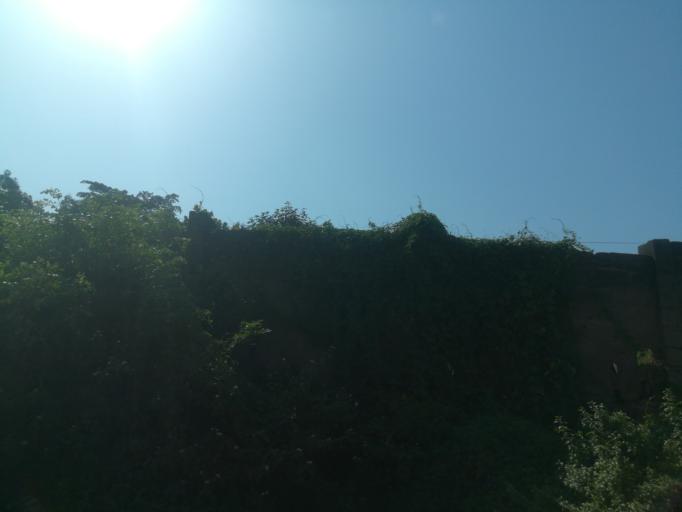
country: NG
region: Ogun
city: Abeokuta
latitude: 7.1497
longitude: 3.3393
